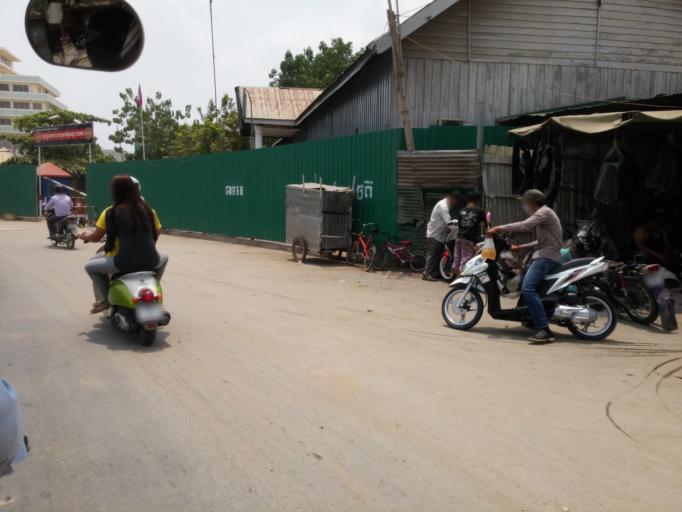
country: KH
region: Phnom Penh
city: Phnom Penh
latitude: 11.5605
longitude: 104.9142
